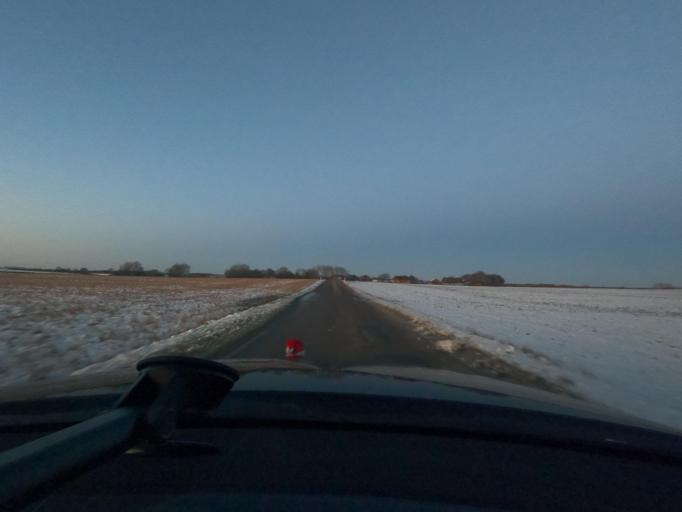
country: DK
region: South Denmark
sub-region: Sonderborg Kommune
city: Horuphav
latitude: 54.8638
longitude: 9.9483
